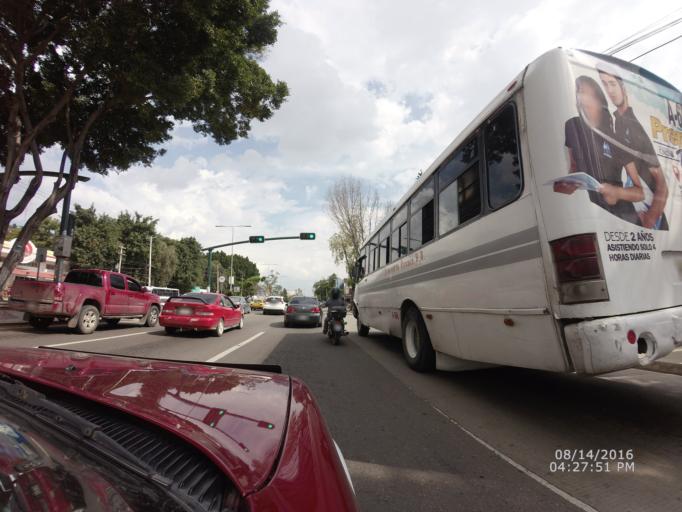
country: MX
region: Oaxaca
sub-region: Santa Maria Atzompa
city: San Jeronimo Yahuiche
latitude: 17.0910
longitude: -96.7473
